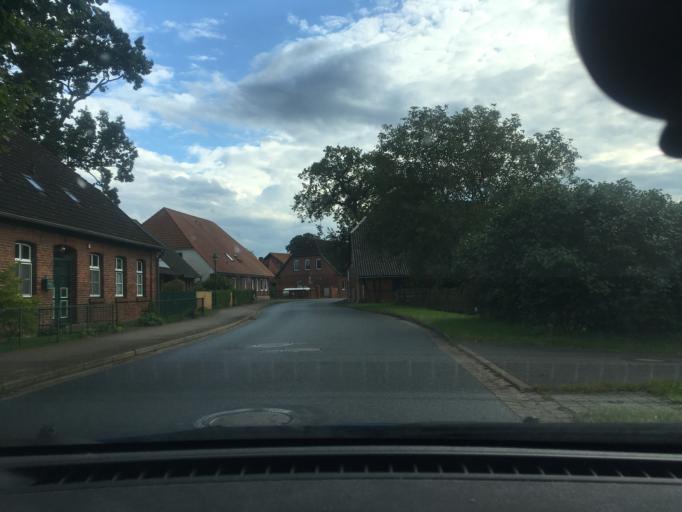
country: DE
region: Lower Saxony
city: Neu Darchau
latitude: 53.2877
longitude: 10.9301
